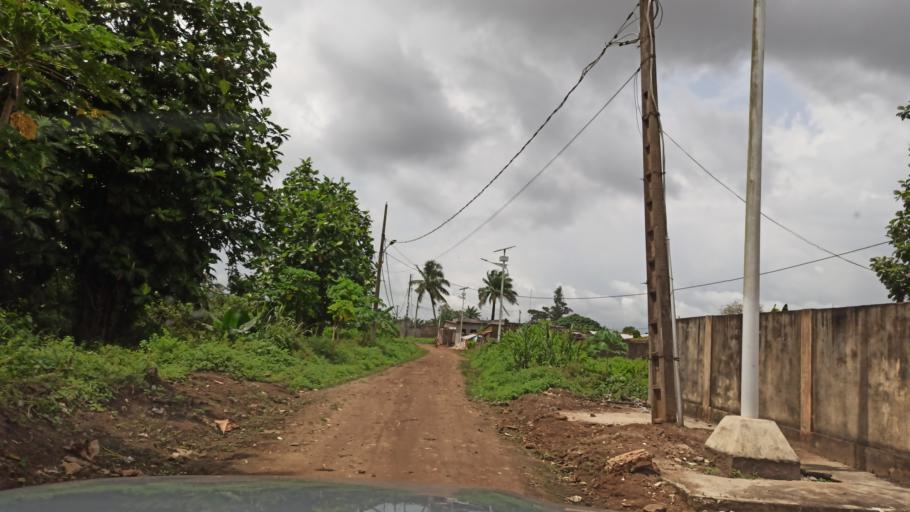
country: BJ
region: Queme
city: Porto-Novo
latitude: 6.4667
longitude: 2.6336
